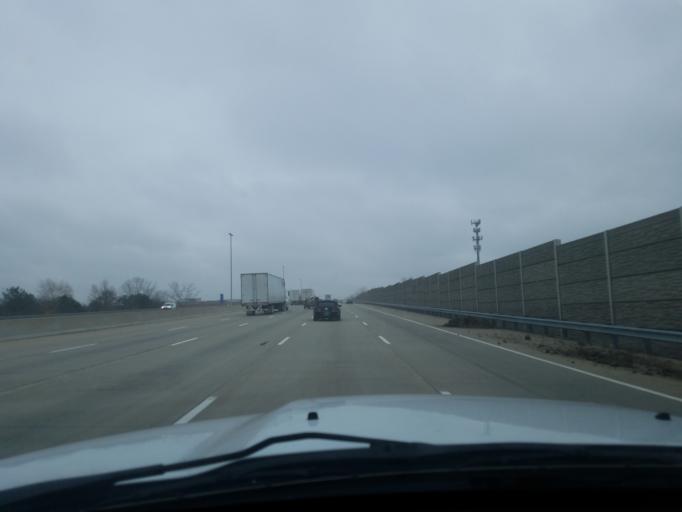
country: US
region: Indiana
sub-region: Marion County
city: Meridian Hills
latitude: 39.9277
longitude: -86.1331
